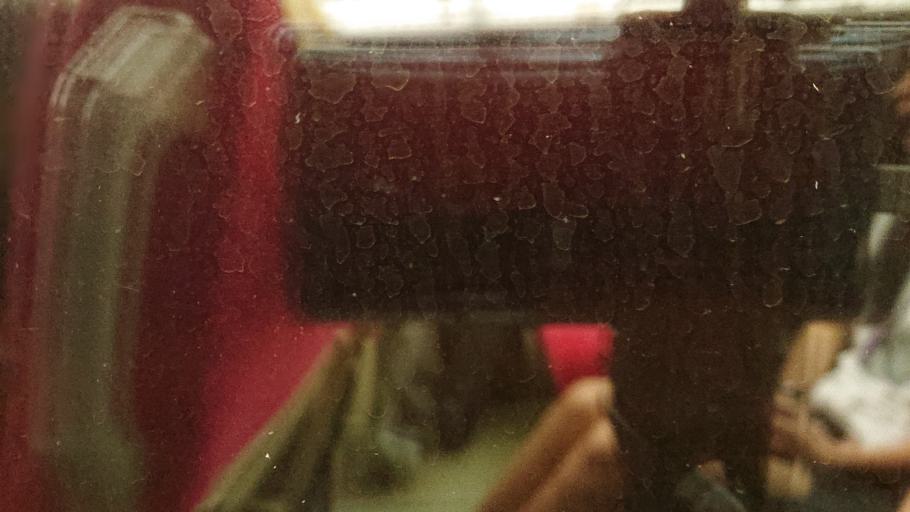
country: TW
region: Taiwan
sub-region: Yilan
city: Yilan
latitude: 24.9328
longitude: 121.8833
